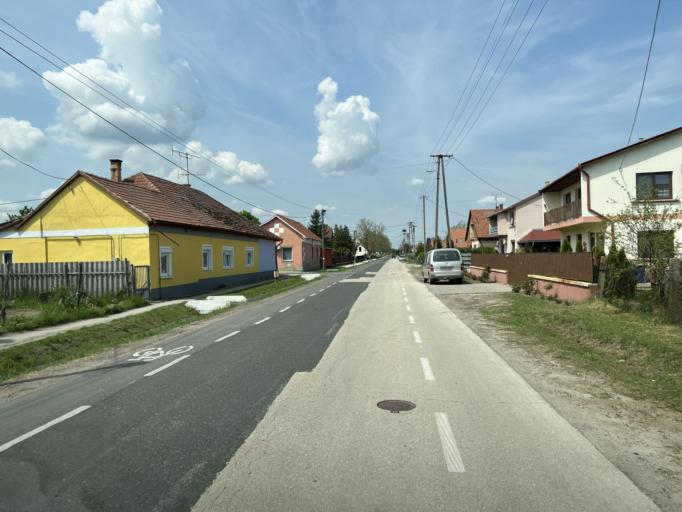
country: HU
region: Pest
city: Nagykoros
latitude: 47.1013
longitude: 19.8016
